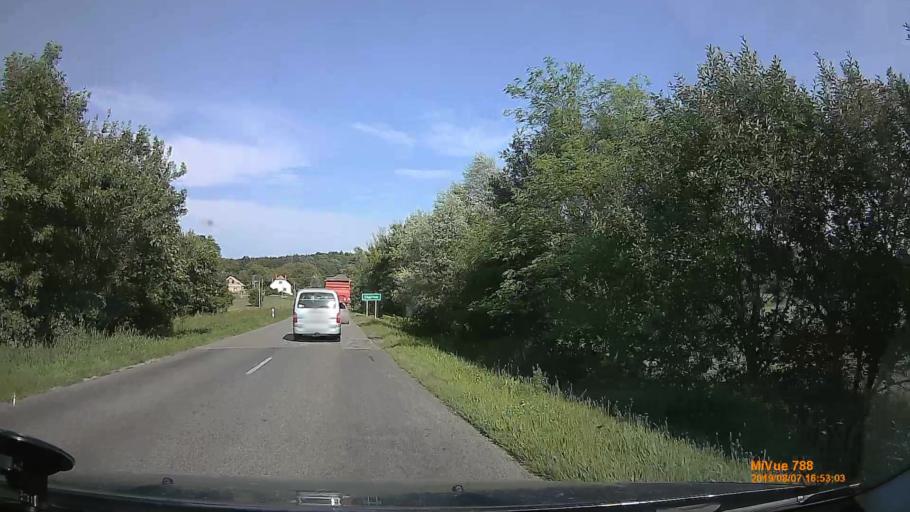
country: HU
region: Zala
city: Lenti
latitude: 46.6857
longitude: 16.7005
